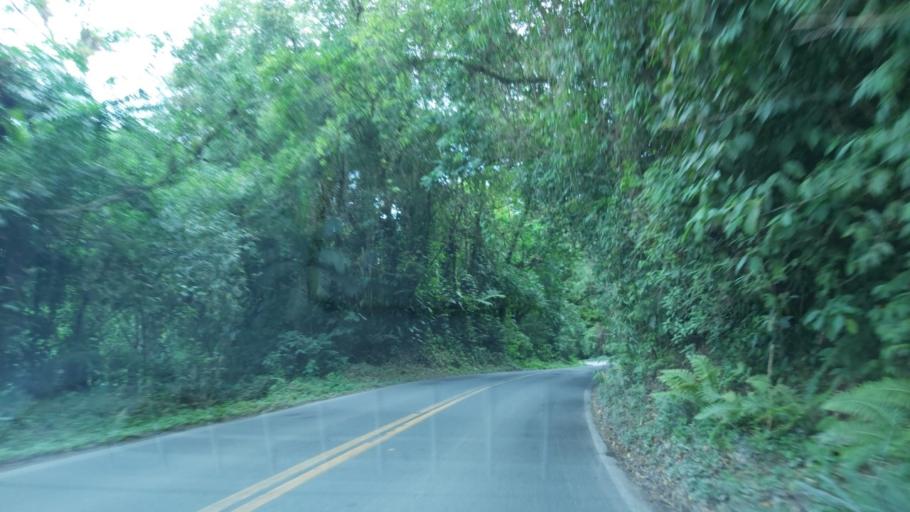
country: BR
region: Sao Paulo
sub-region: Juquia
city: Juquia
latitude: -24.0747
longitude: -47.6041
